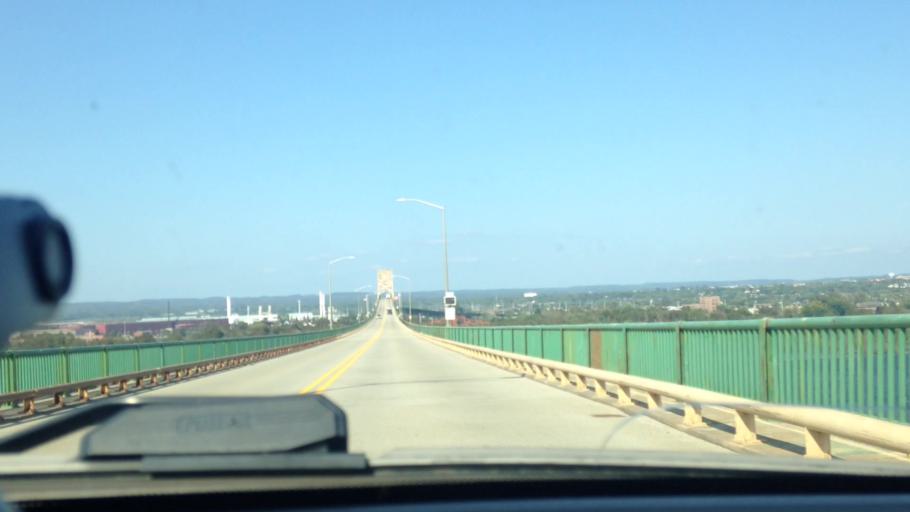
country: US
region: Michigan
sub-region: Chippewa County
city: Sault Ste. Marie
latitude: 46.5055
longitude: -84.3623
